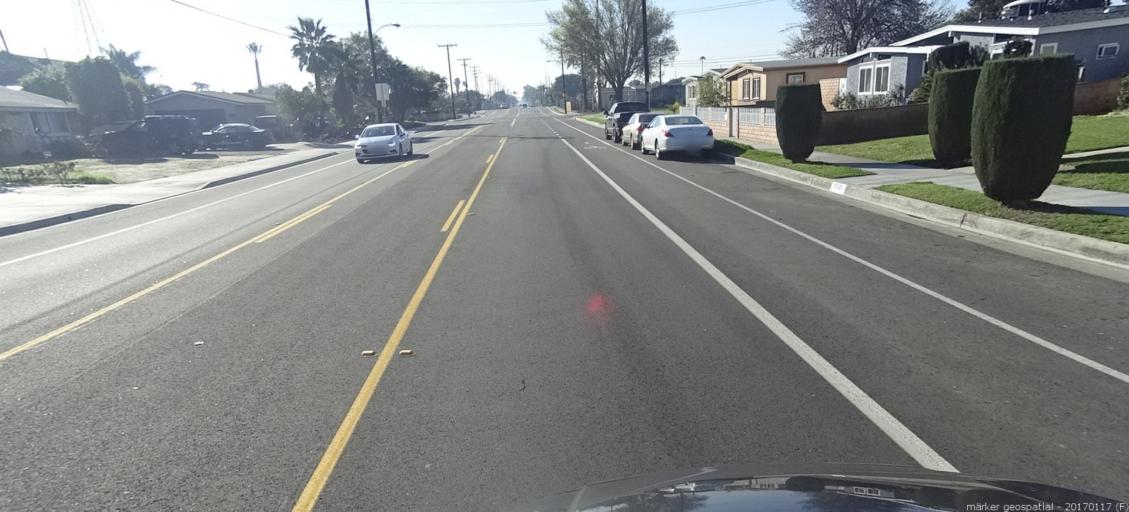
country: US
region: California
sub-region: Orange County
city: Stanton
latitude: 33.8088
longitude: -117.9676
